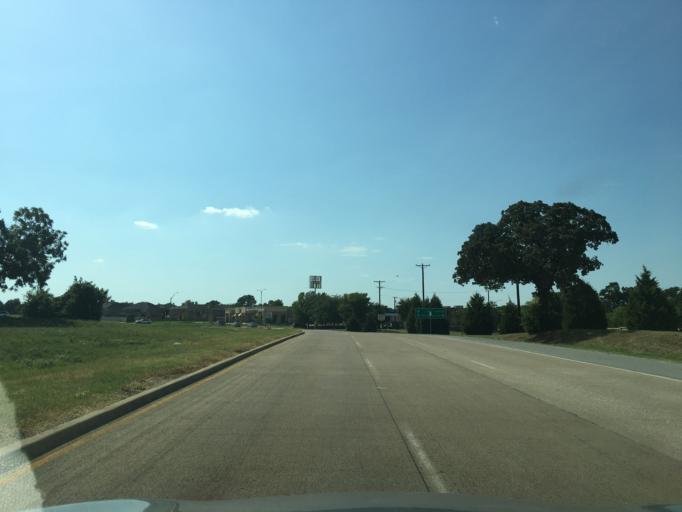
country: US
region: Texas
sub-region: Tarrant County
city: Dalworthington Gardens
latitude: 32.6761
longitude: -97.1647
